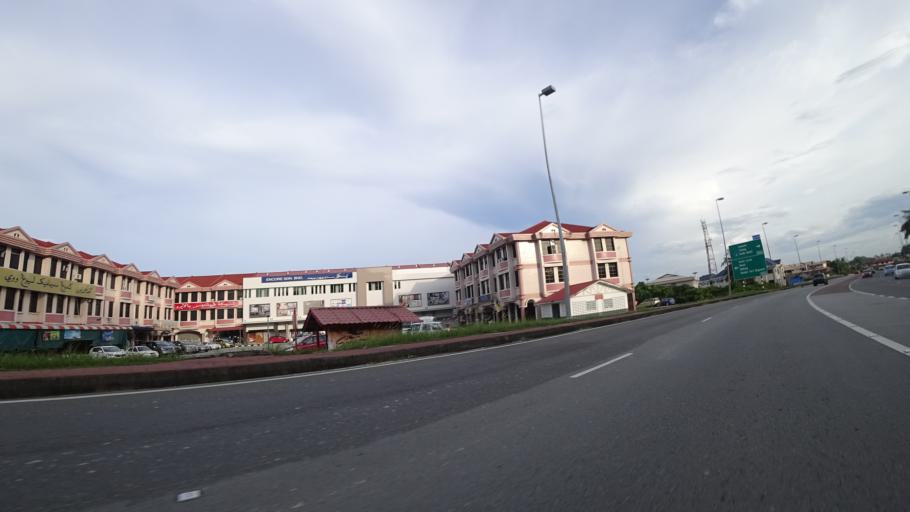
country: BN
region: Brunei and Muara
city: Bandar Seri Begawan
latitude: 4.8886
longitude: 114.8382
